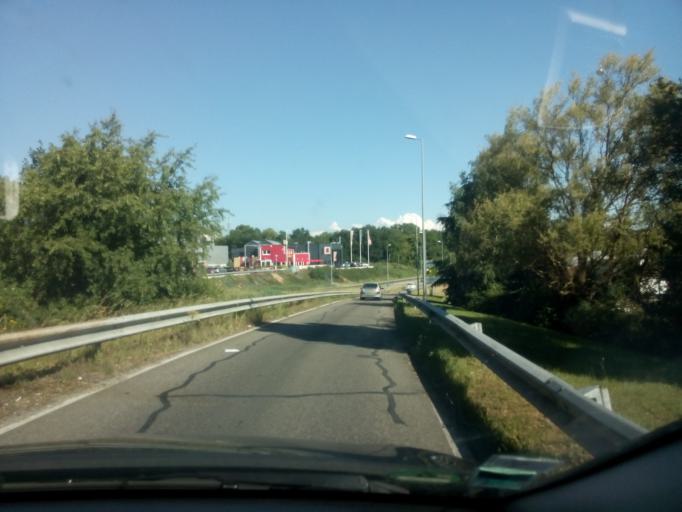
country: FR
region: Alsace
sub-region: Departement du Bas-Rhin
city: Kaltenhouse
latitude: 48.8009
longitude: 7.8344
